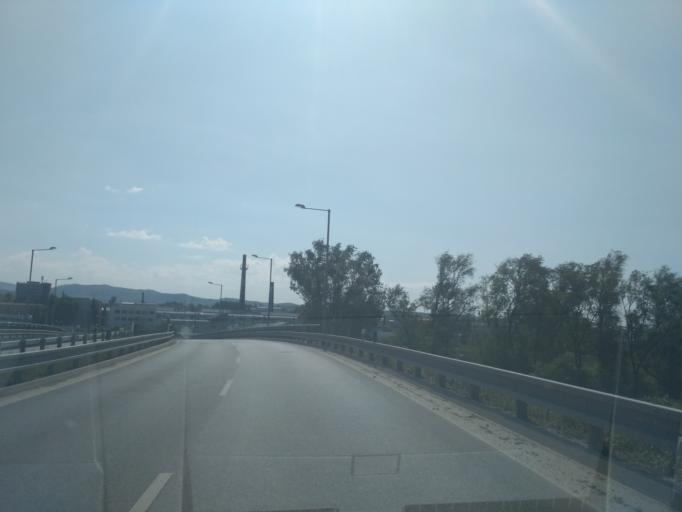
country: SK
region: Presovsky
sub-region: Okres Presov
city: Presov
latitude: 48.9696
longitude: 21.2483
